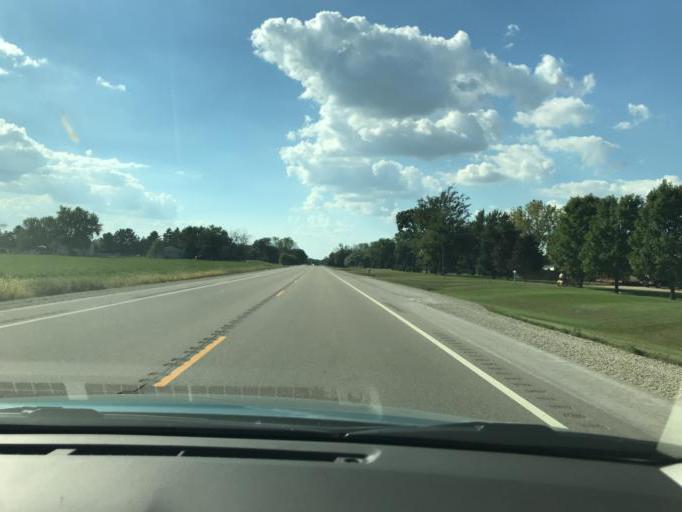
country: US
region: Wisconsin
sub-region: Green County
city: Brodhead
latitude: 42.5722
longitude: -89.3531
